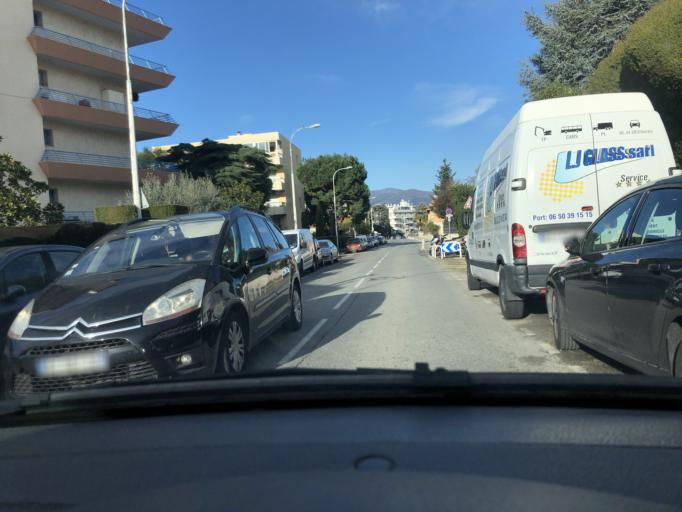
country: FR
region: Provence-Alpes-Cote d'Azur
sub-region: Departement des Alpes-Maritimes
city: Saint-Laurent-du-Var
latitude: 43.6802
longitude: 7.2091
